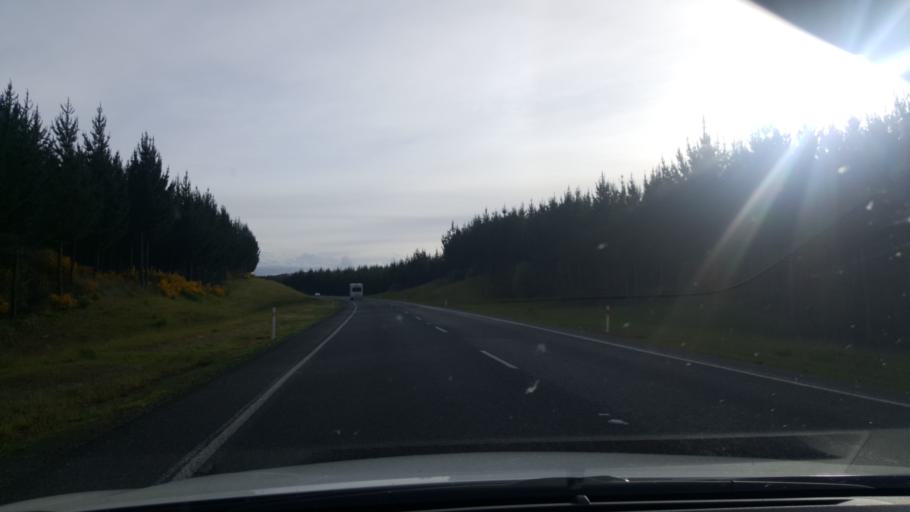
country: NZ
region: Waikato
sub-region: Taupo District
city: Taupo
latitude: -38.8244
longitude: 176.0702
